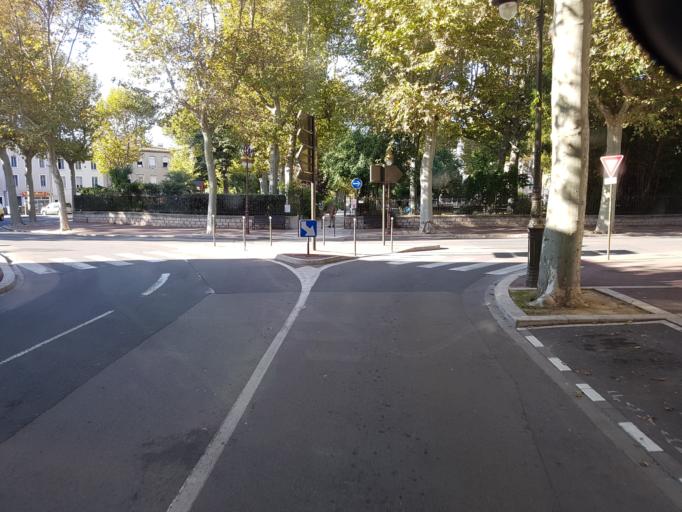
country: FR
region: Languedoc-Roussillon
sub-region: Departement de l'Aude
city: Narbonne
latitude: 43.1868
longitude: 3.0085
